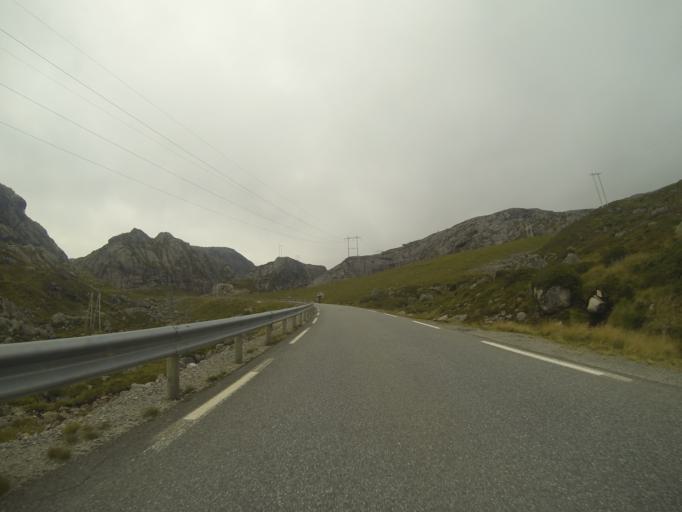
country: NO
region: Vest-Agder
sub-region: Sirdal
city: Tonstad
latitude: 59.0335
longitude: 6.6528
